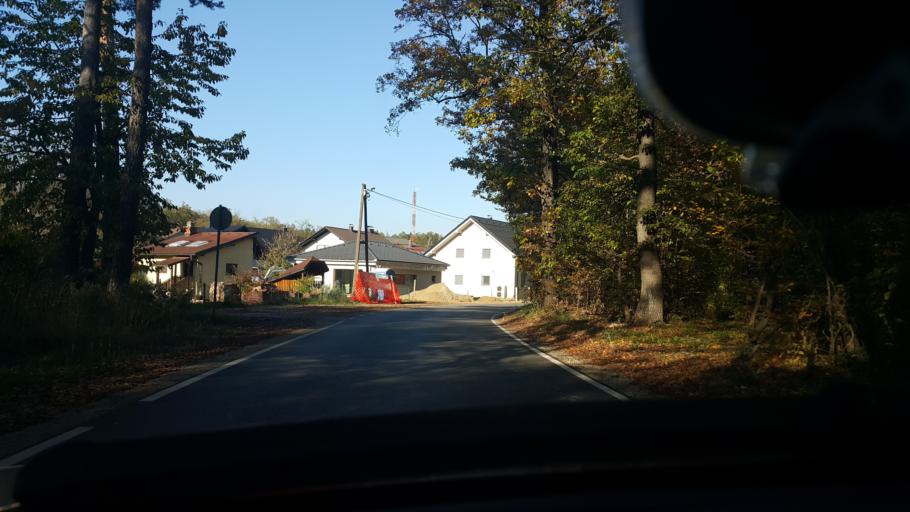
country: SI
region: Miklavz na Dravskem Polju
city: Miklavz na Dravskem Polju
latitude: 46.5325
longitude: 15.6848
